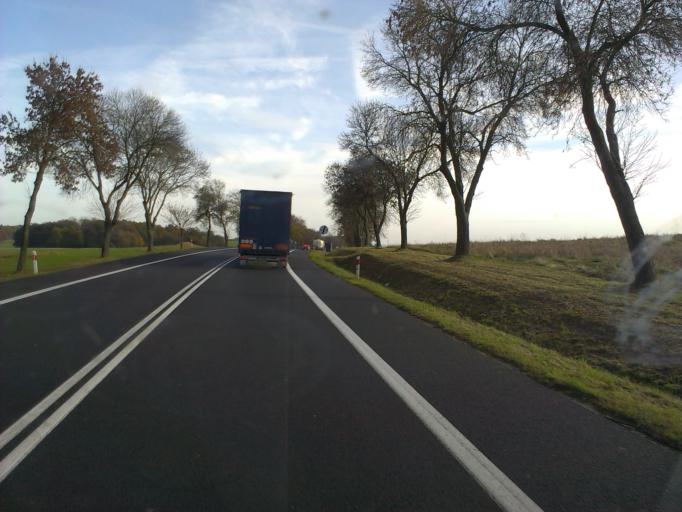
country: PL
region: Lower Silesian Voivodeship
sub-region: Powiat polkowicki
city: Gaworzyce
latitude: 51.6445
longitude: 15.8708
